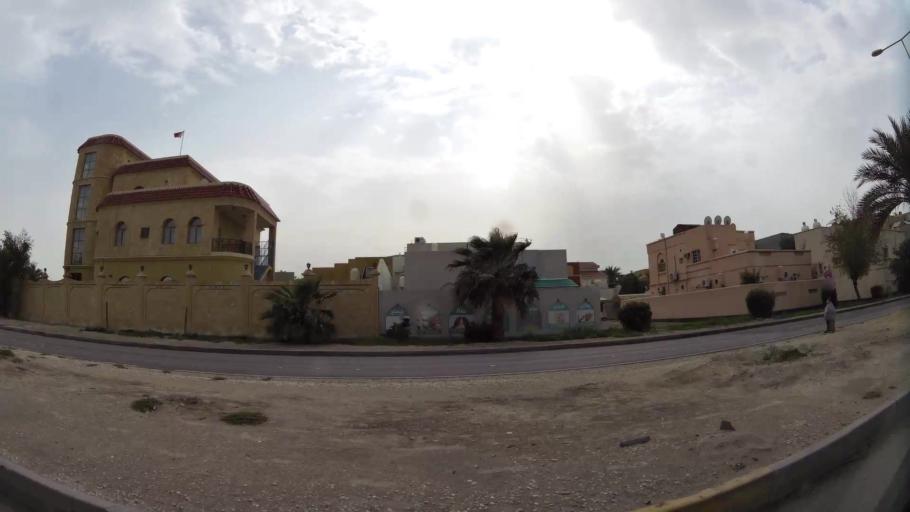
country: BH
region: Northern
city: Ar Rifa'
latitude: 26.1342
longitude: 50.5715
